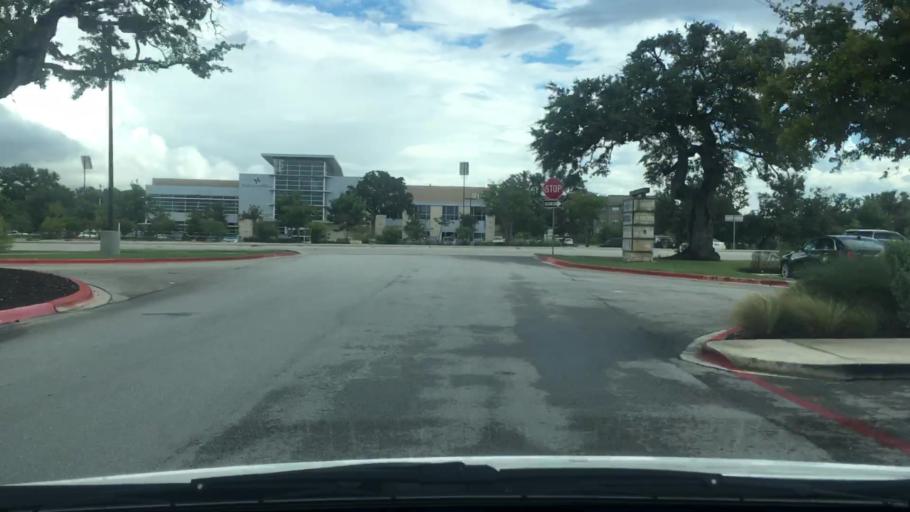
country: US
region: Texas
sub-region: Williamson County
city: Cedar Park
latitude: 30.5249
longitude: -97.8193
